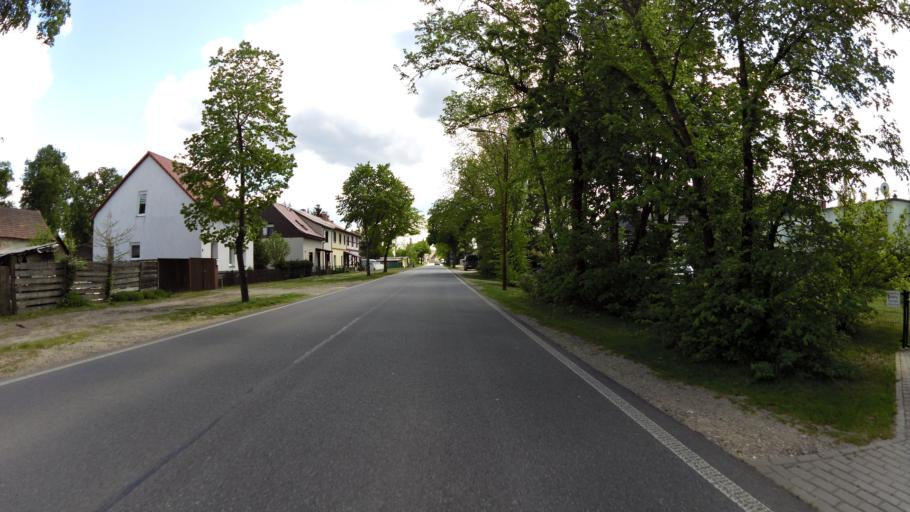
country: DE
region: Brandenburg
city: Halbe
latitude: 52.1082
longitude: 13.6915
